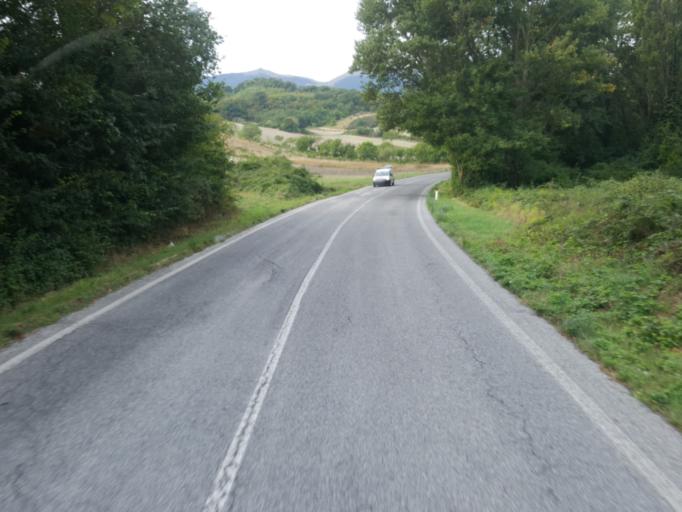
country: IT
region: The Marches
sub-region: Provincia di Ancona
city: Fabriano
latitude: 43.3143
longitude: 12.8359
